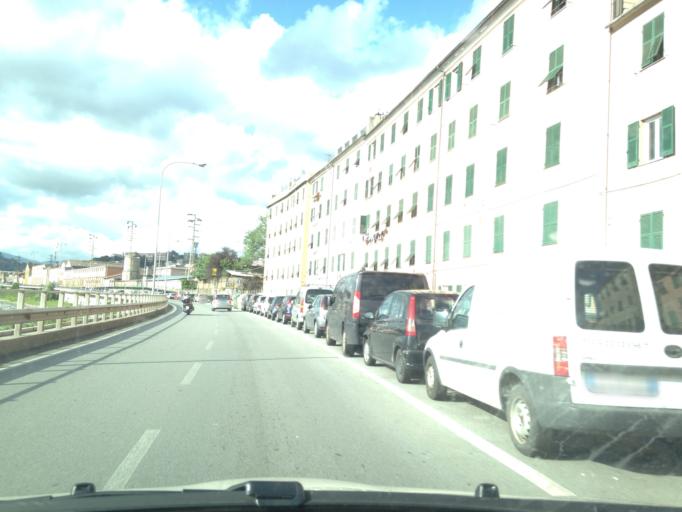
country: IT
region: Liguria
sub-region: Provincia di Genova
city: San Teodoro
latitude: 44.4287
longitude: 8.8898
